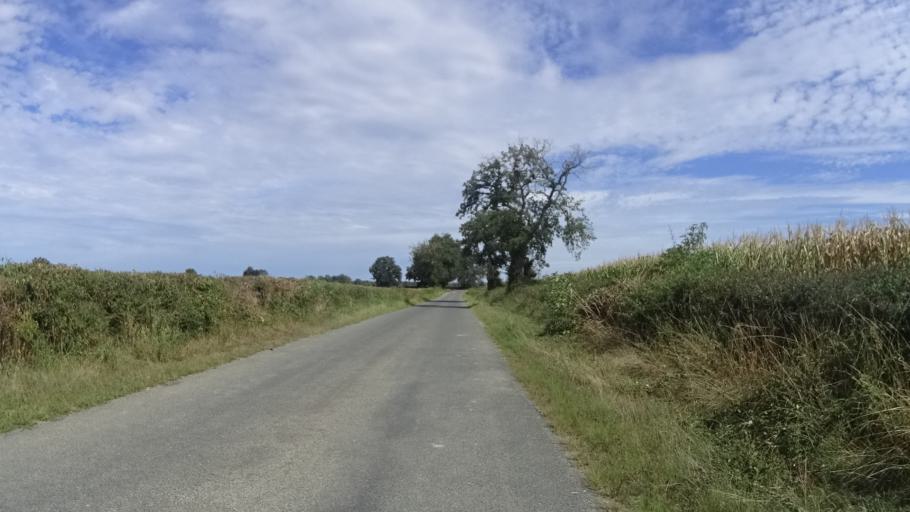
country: FR
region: Auvergne
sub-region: Departement de l'Allier
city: Beaulon
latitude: 46.6364
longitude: 3.6942
